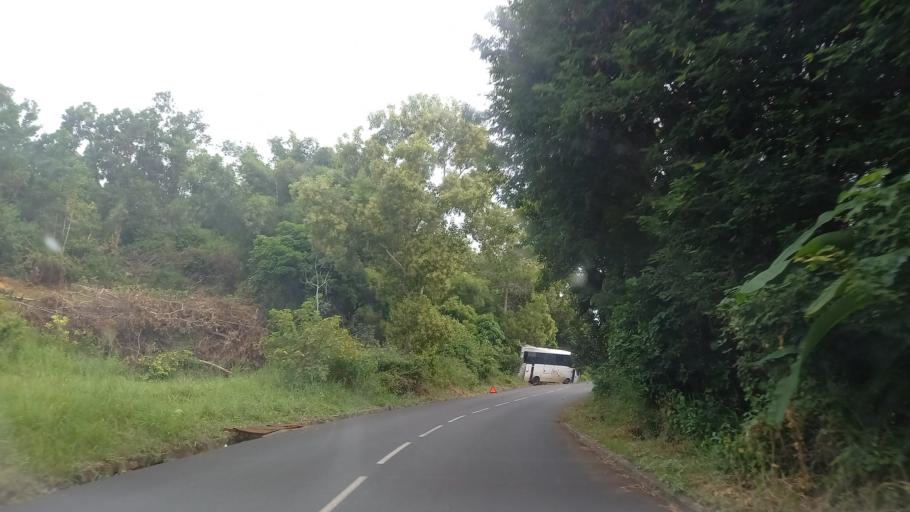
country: YT
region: Boueni
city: Boueni
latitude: -12.9010
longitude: 45.0900
